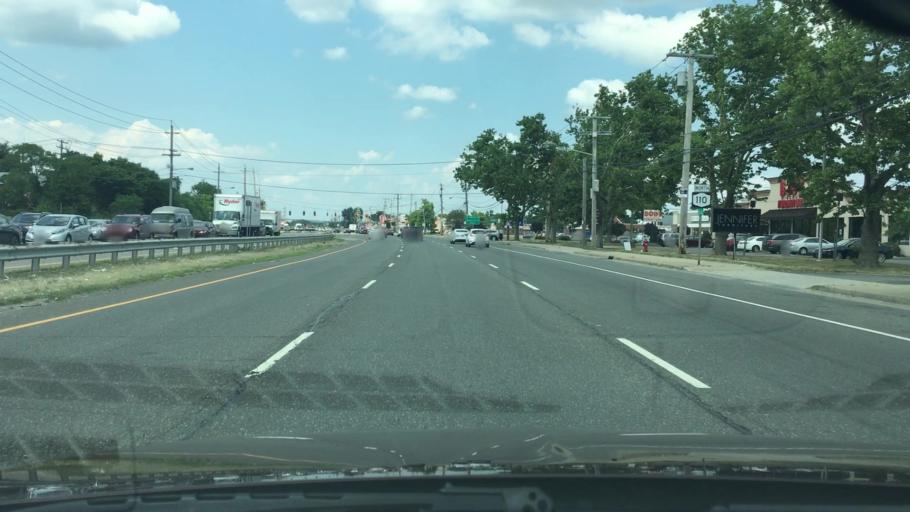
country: US
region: New York
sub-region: Suffolk County
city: East Farmingdale
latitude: 40.7475
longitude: -73.4221
